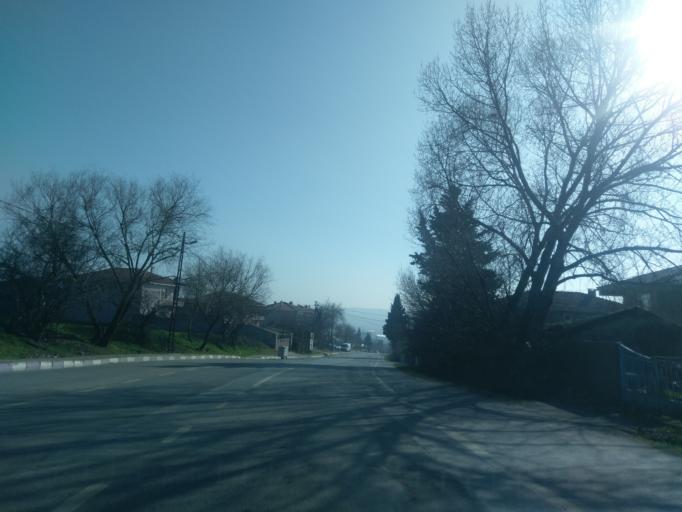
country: TR
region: Istanbul
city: Catalca
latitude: 41.1211
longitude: 28.4509
